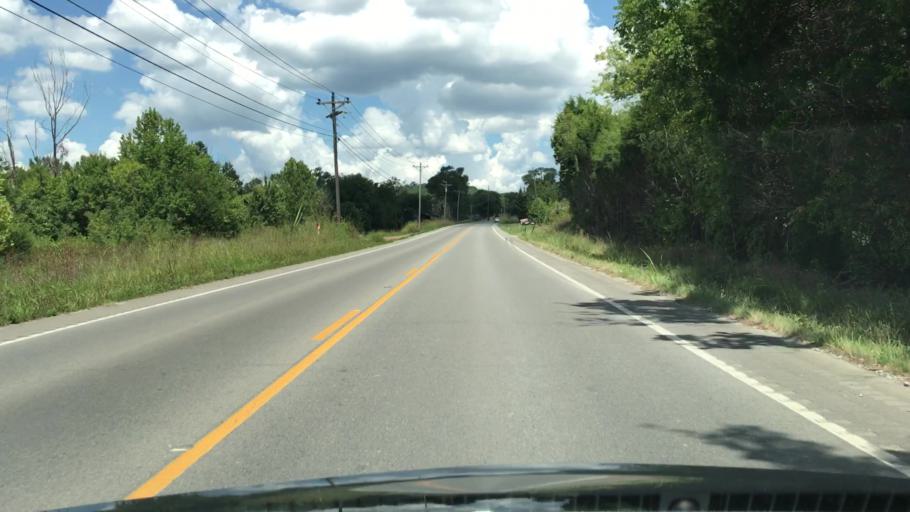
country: US
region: Tennessee
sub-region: Williamson County
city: Nolensville
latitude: 35.8926
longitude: -86.6655
